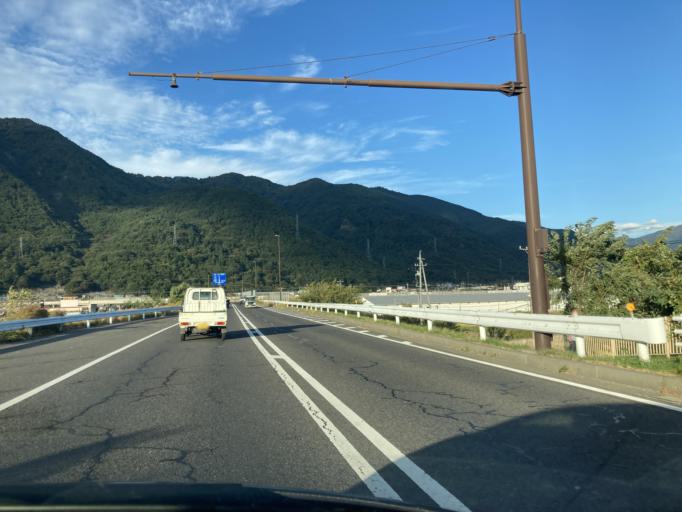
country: JP
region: Nagano
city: Ueda
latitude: 36.4119
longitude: 138.2183
